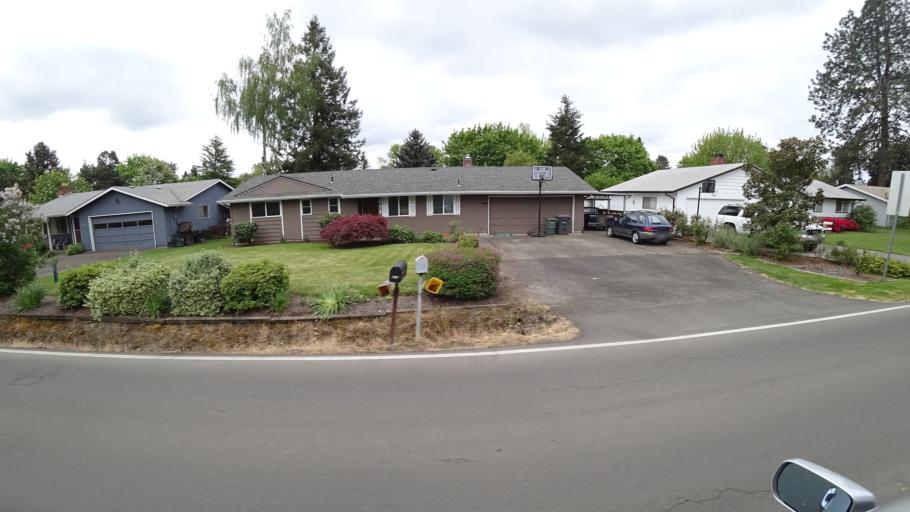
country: US
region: Oregon
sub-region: Washington County
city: Hillsboro
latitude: 45.5366
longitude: -122.9736
